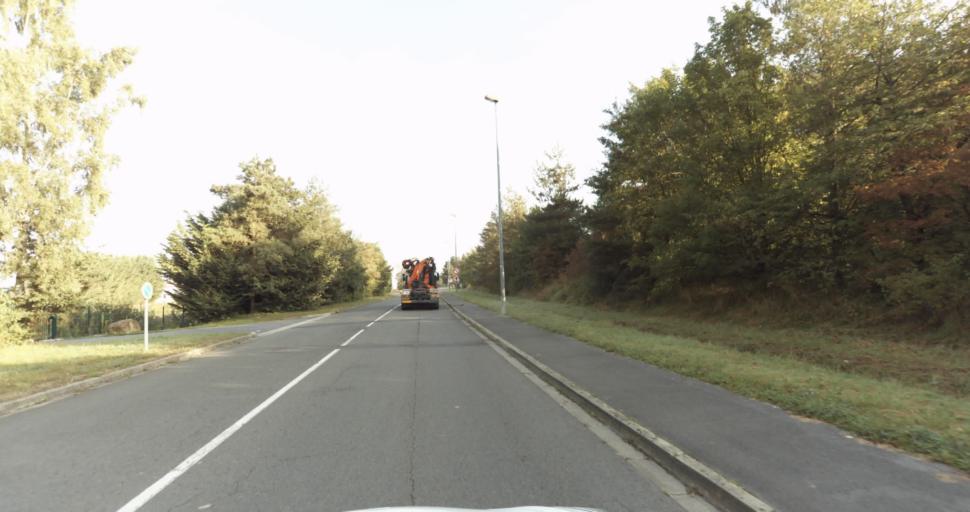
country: FR
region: Champagne-Ardenne
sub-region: Departement des Ardennes
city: Villers-Semeuse
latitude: 49.7302
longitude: 4.7572
